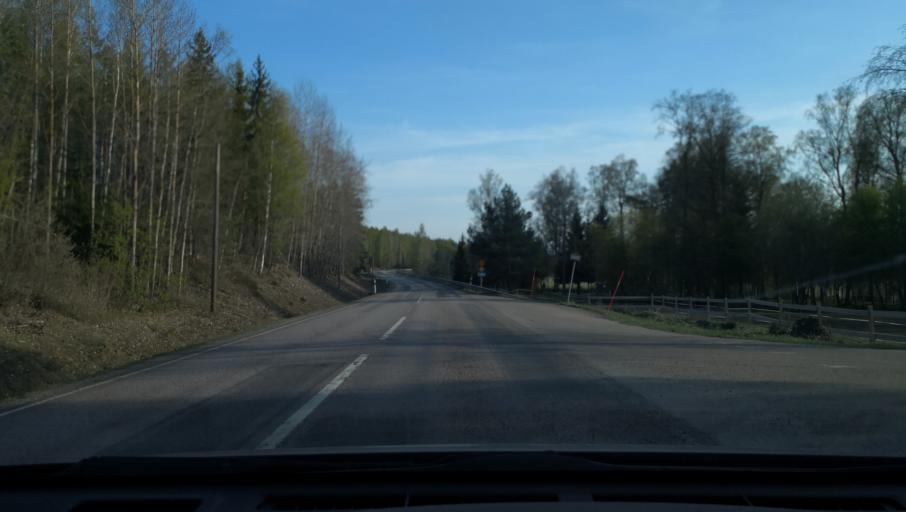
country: SE
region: Uppsala
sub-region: Heby Kommun
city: Heby
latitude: 59.9993
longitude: 16.8322
